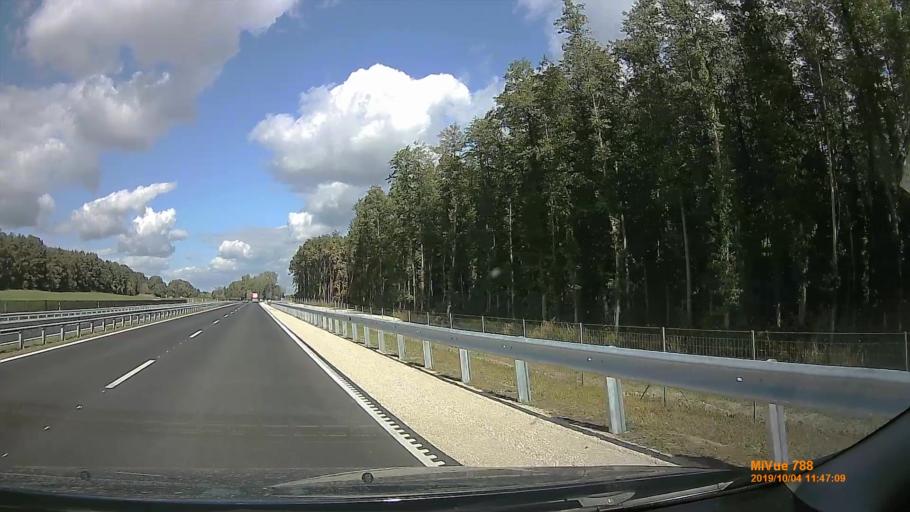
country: HU
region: Somogy
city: Karad
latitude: 46.6453
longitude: 17.7870
